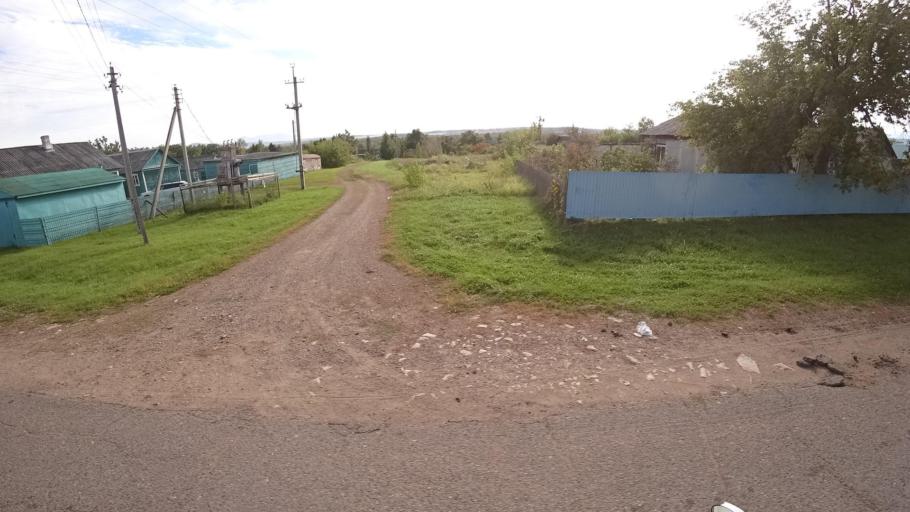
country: RU
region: Primorskiy
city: Dostoyevka
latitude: 44.3003
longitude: 133.4498
